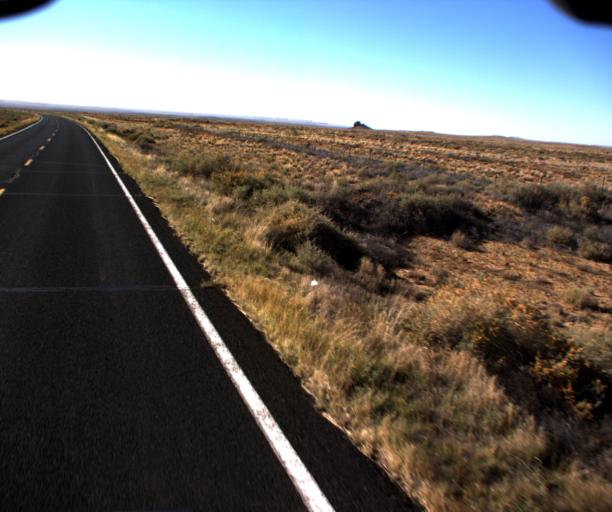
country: US
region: Arizona
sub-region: Navajo County
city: First Mesa
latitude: 35.7403
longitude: -110.5188
